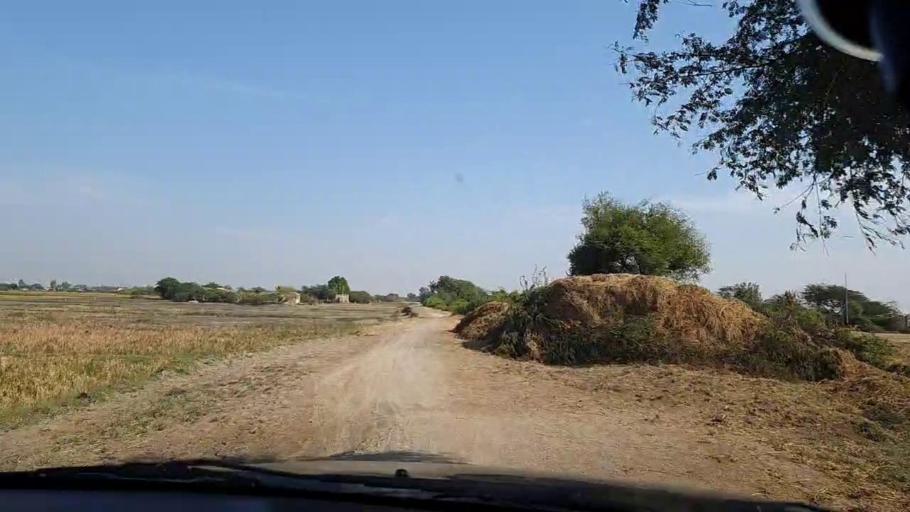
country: PK
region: Sindh
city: Mirpur Batoro
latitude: 24.6286
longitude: 68.2697
